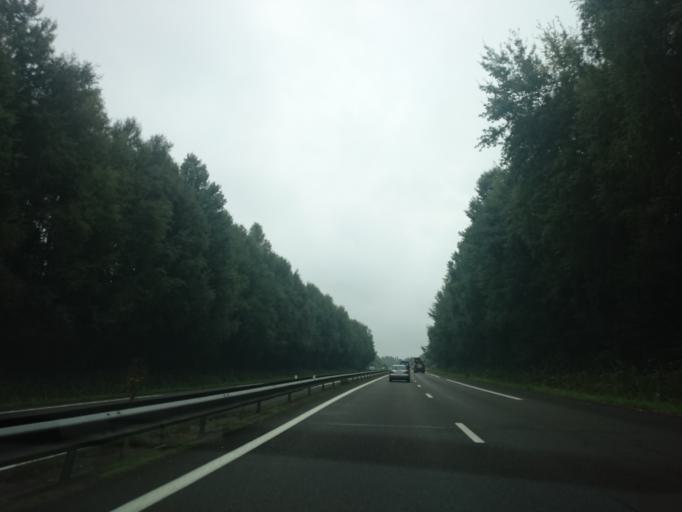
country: FR
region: Pays de la Loire
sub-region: Departement de la Loire-Atlantique
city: Treillieres
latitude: 47.3200
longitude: -1.6439
